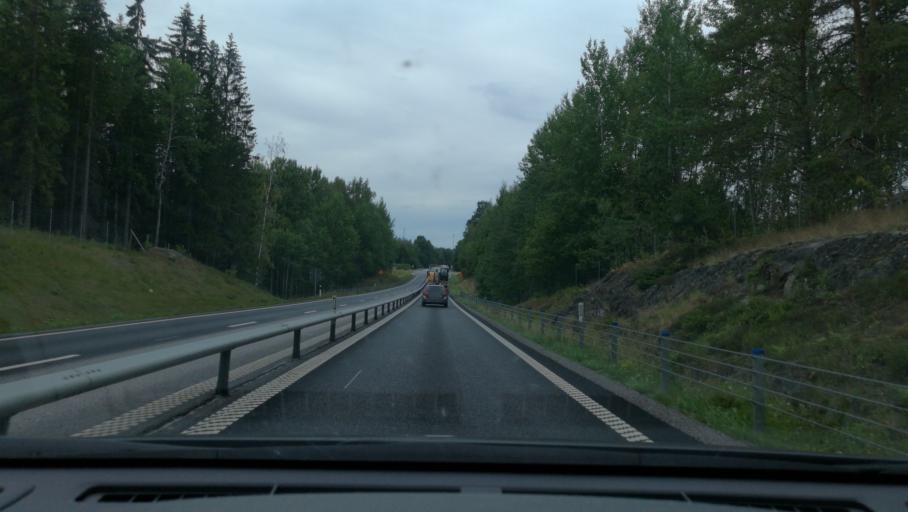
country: SE
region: Soedermanland
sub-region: Katrineholms Kommun
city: Katrineholm
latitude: 58.9022
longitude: 16.2053
